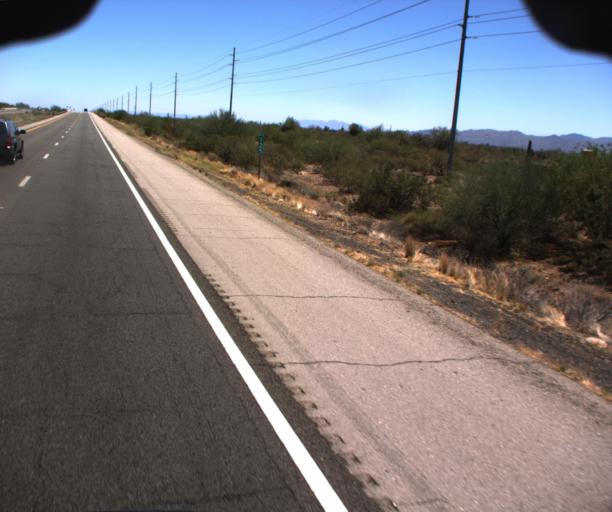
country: US
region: Arizona
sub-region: Maricopa County
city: Wickenburg
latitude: 33.8147
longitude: -112.5761
